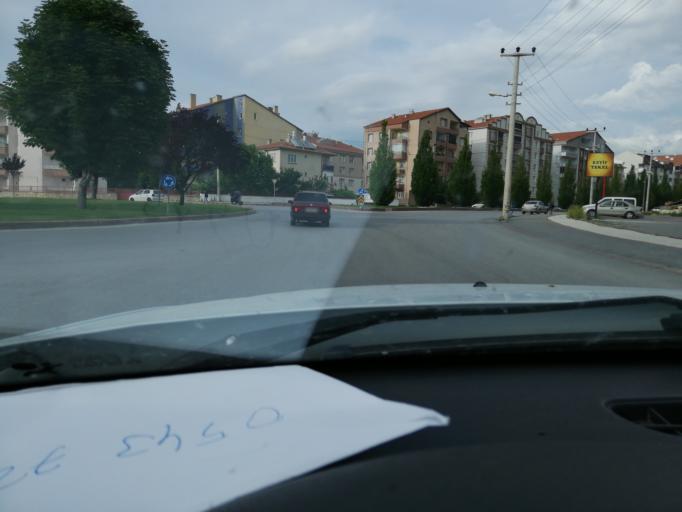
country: TR
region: Kirsehir
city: Kirsehir
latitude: 39.1347
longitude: 34.1597
